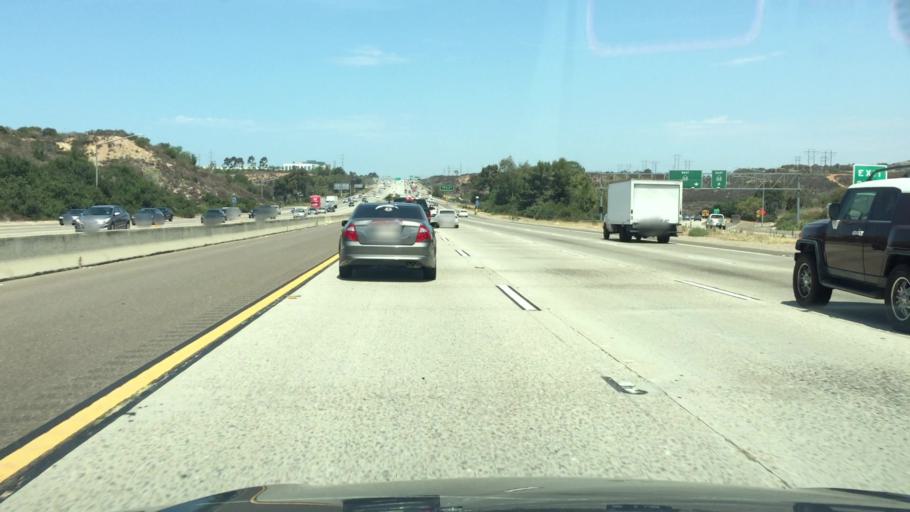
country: US
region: California
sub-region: San Diego County
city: La Jolla
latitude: 32.8427
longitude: -117.1751
